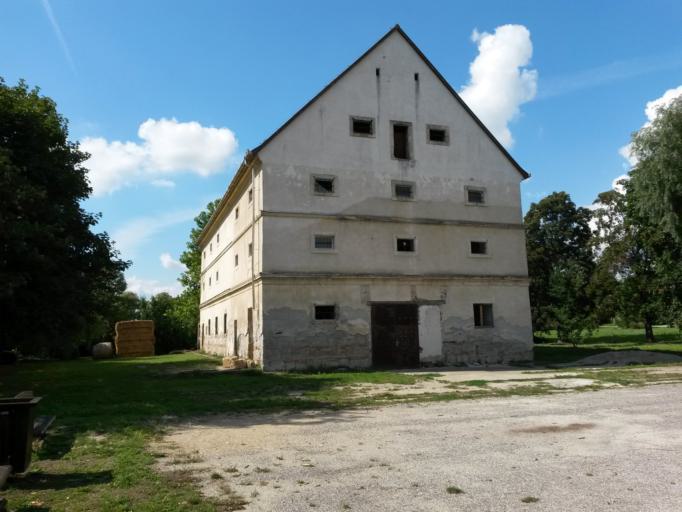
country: HU
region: Pest
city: Telki
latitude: 47.5575
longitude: 18.7986
